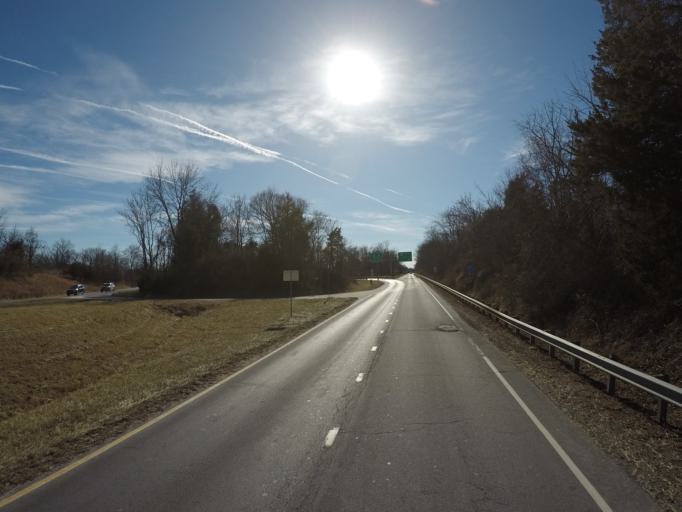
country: US
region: Virginia
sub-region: Loudoun County
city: Leesburg
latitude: 39.1389
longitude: -77.5476
